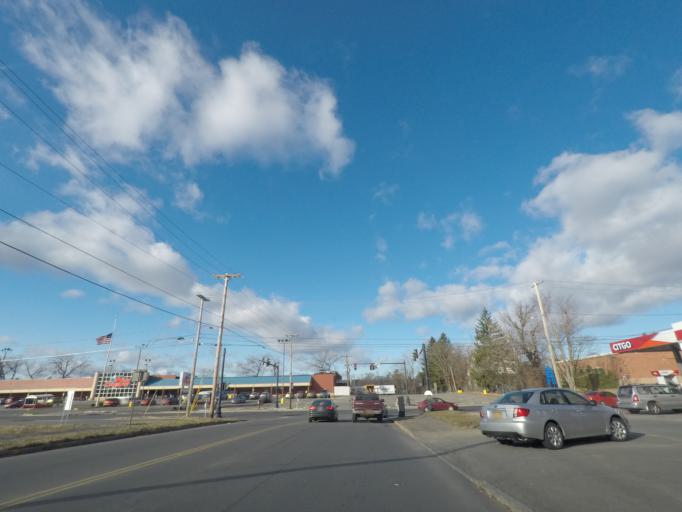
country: US
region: New York
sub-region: Saratoga County
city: Waterford
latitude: 42.7866
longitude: -73.6712
